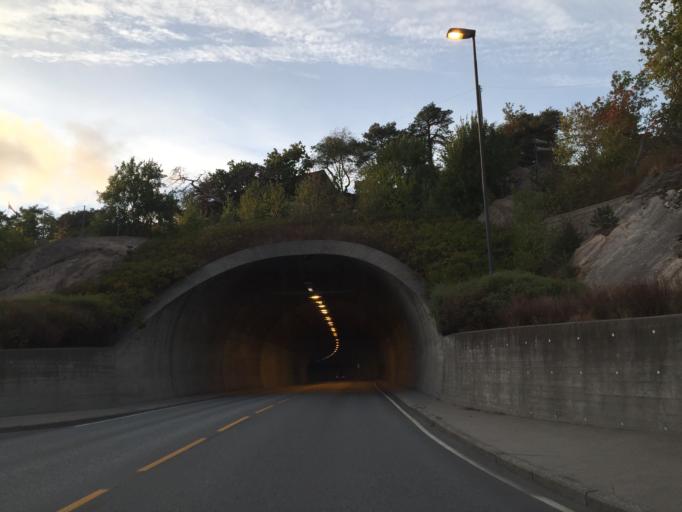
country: NO
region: Ostfold
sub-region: Fredrikstad
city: Fredrikstad
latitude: 59.2072
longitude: 10.9367
